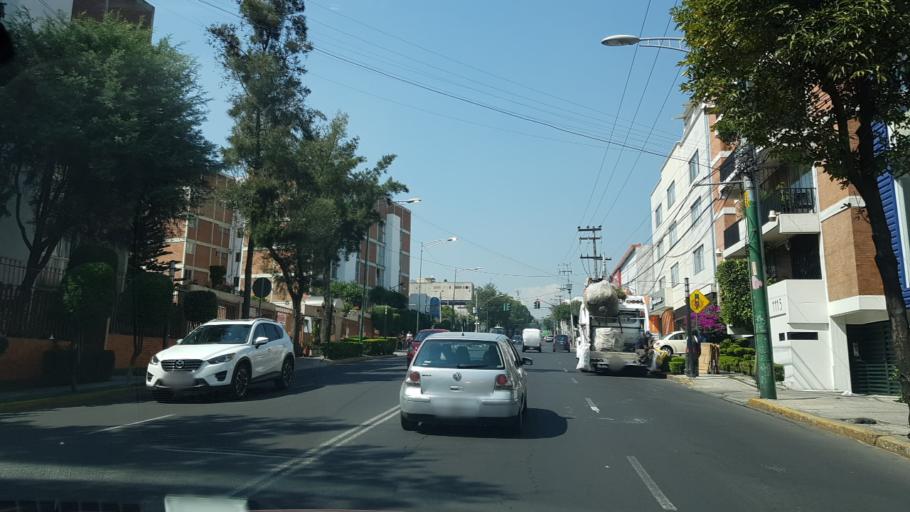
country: MX
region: Mexico City
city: Magdalena Contreras
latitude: 19.3494
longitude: -99.2246
